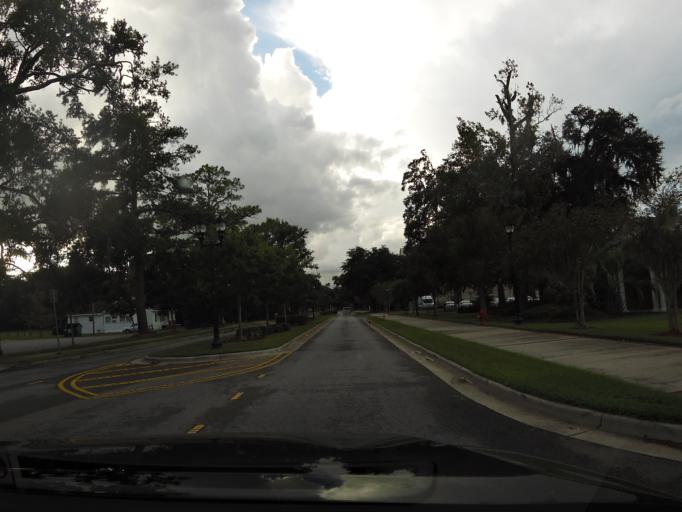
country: US
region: Georgia
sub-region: Liberty County
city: Hinesville
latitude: 31.8491
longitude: -81.5906
